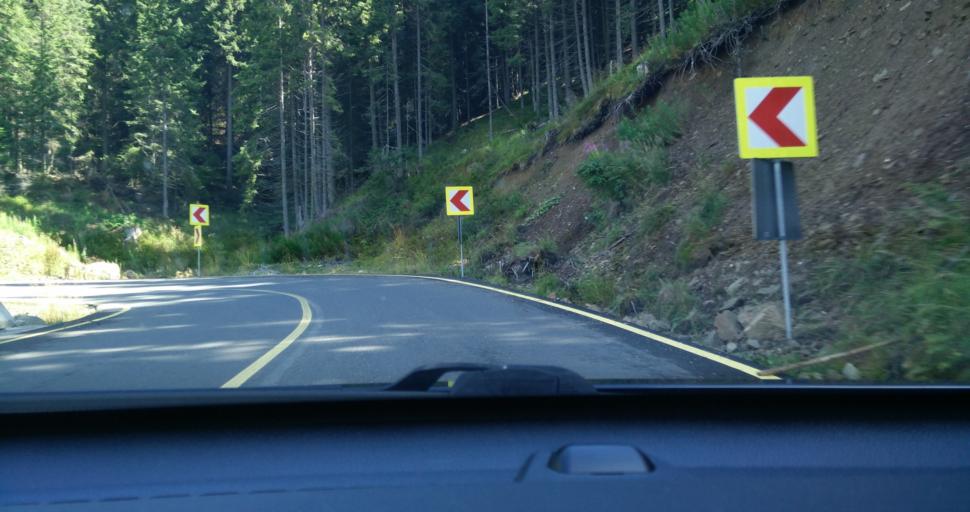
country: RO
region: Hunedoara
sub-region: Oras Petrila
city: Petrila
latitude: 45.4536
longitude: 23.6167
